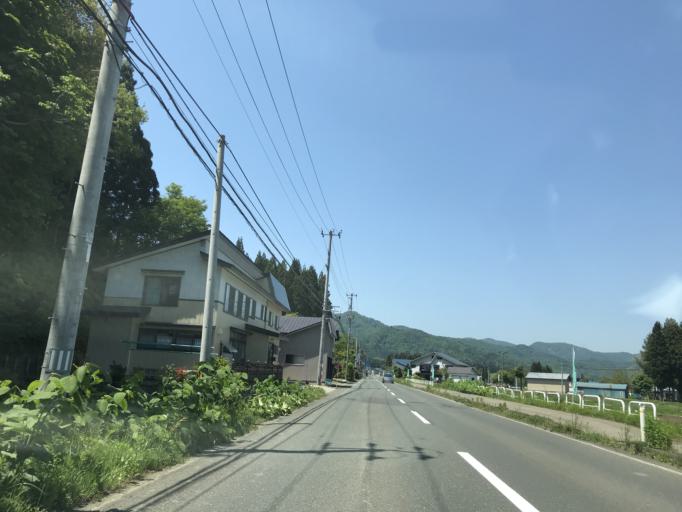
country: JP
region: Akita
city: Yokotemachi
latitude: 39.4049
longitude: 140.7534
